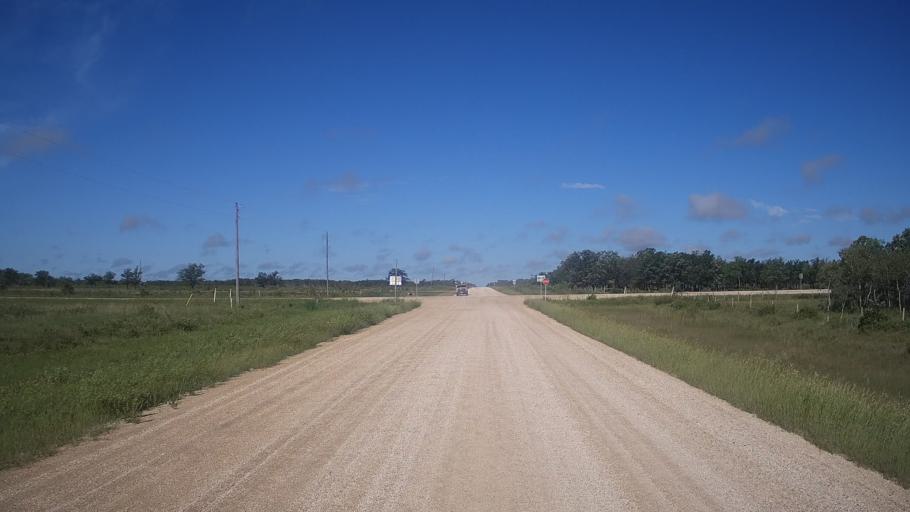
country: CA
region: Manitoba
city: Stonewall
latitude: 50.2411
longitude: -97.7345
